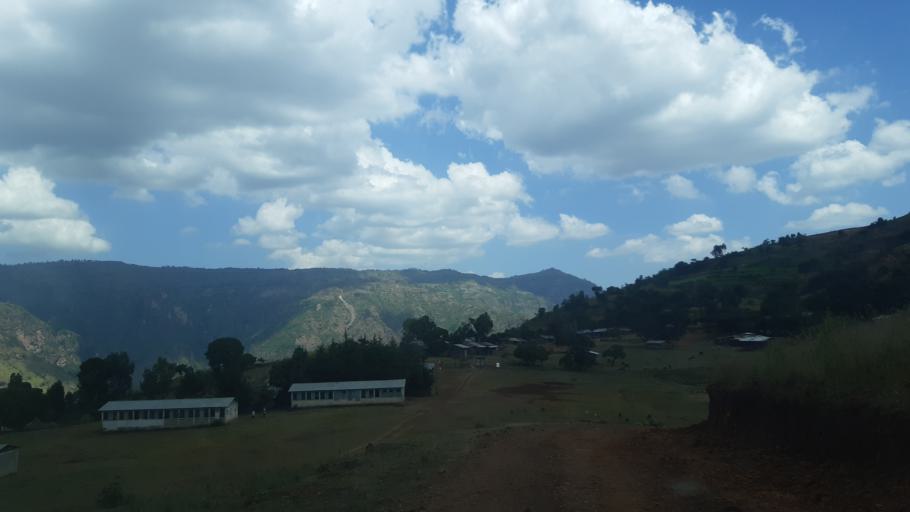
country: ET
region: Amhara
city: Dabat
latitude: 13.3379
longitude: 37.4209
